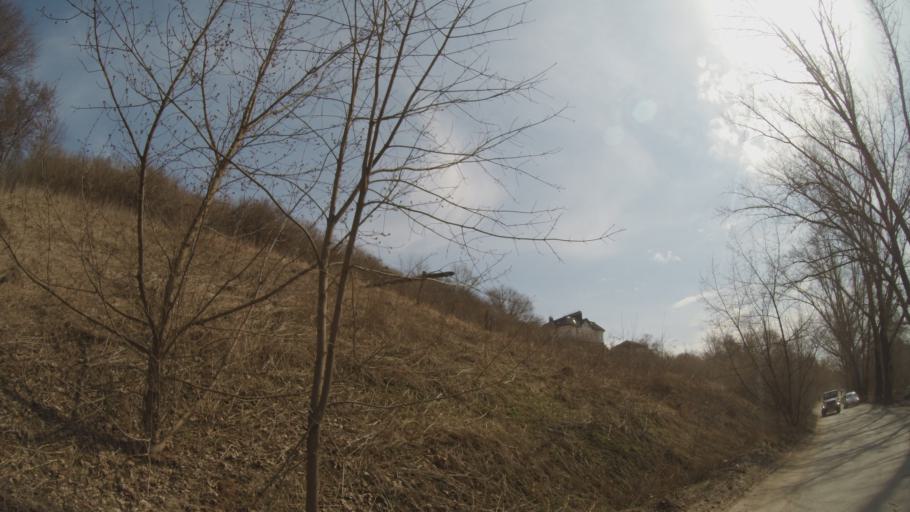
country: RU
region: Nizjnij Novgorod
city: Vyyezdnoye
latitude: 55.3909
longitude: 43.8083
